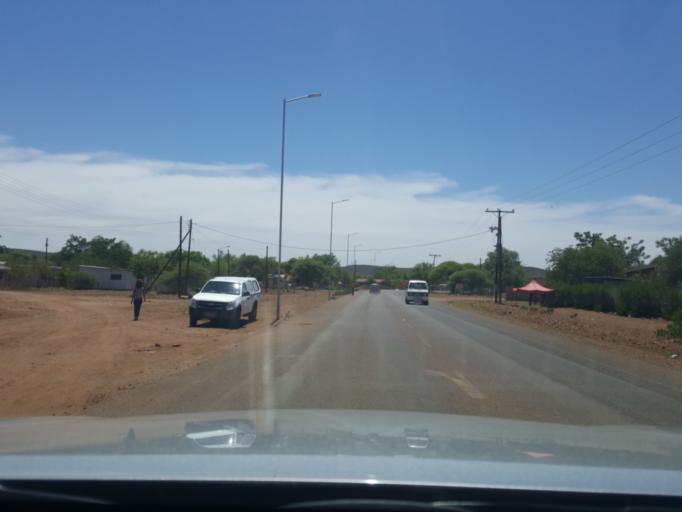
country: BW
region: South East
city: Ramotswa
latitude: -24.8683
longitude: 25.8744
